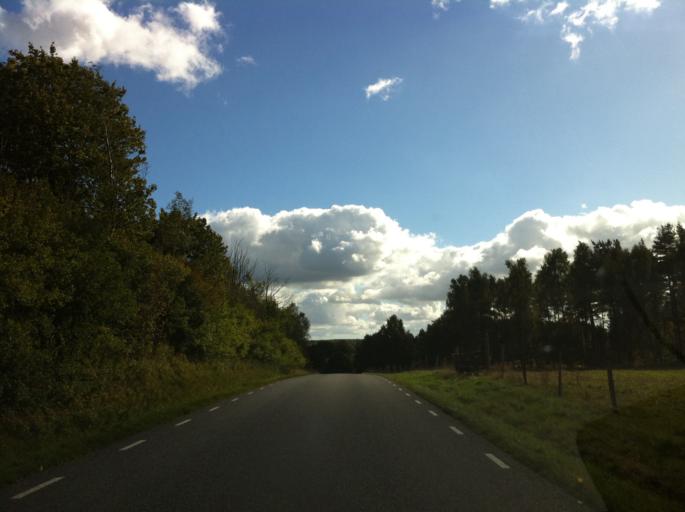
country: SE
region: Skane
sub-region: Kristianstads Kommun
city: Degeberga
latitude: 55.7129
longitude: 13.9751
